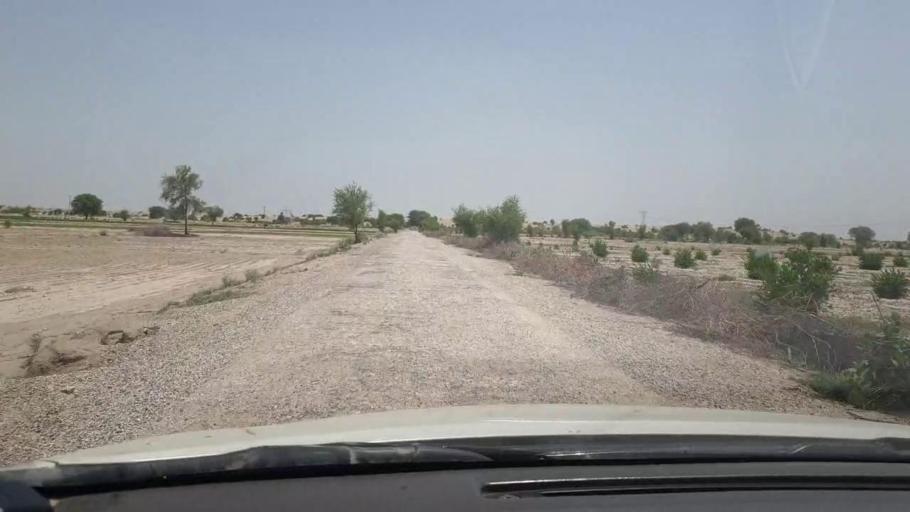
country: PK
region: Sindh
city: Rohri
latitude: 27.5062
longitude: 69.1768
